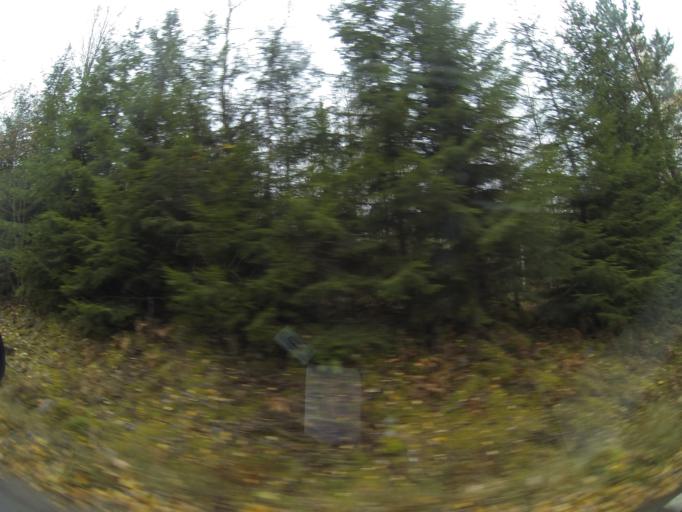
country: SE
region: Vaestmanland
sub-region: Surahammars Kommun
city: Surahammar
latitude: 59.6710
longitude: 16.0777
